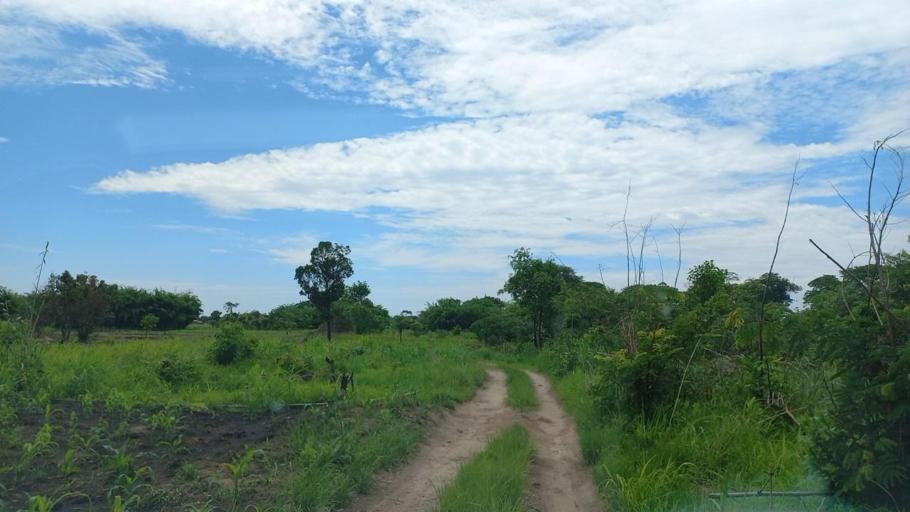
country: ZM
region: Copperbelt
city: Kitwe
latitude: -12.7908
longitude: 28.3986
